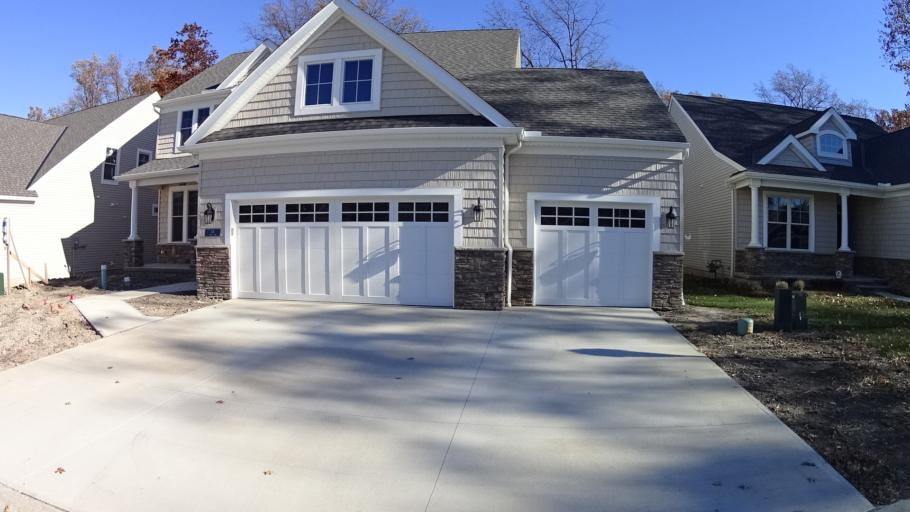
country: US
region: Ohio
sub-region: Lorain County
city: Avon Center
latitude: 41.4806
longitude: -82.0085
